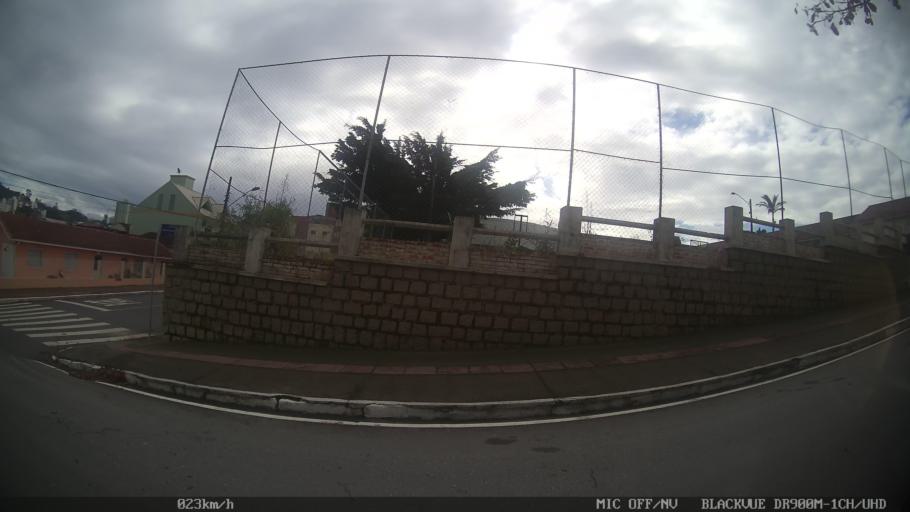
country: BR
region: Santa Catarina
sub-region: Sao Jose
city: Campinas
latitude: -27.5729
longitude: -48.6198
